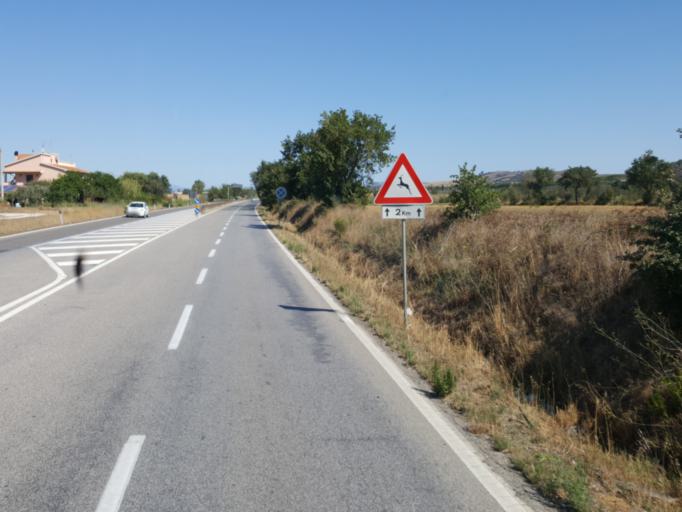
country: IT
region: Tuscany
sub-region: Provincia di Grosseto
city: Grosseto
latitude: 42.6900
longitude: 11.1385
